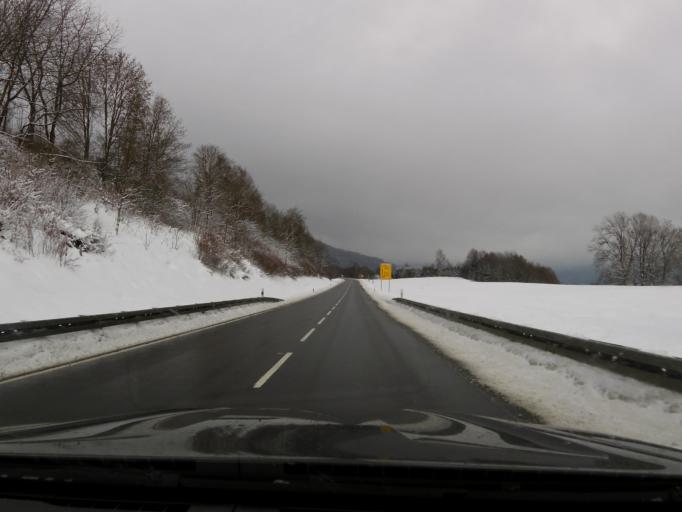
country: DE
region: Bavaria
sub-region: Lower Bavaria
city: Hunding
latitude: 48.8408
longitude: 13.1596
